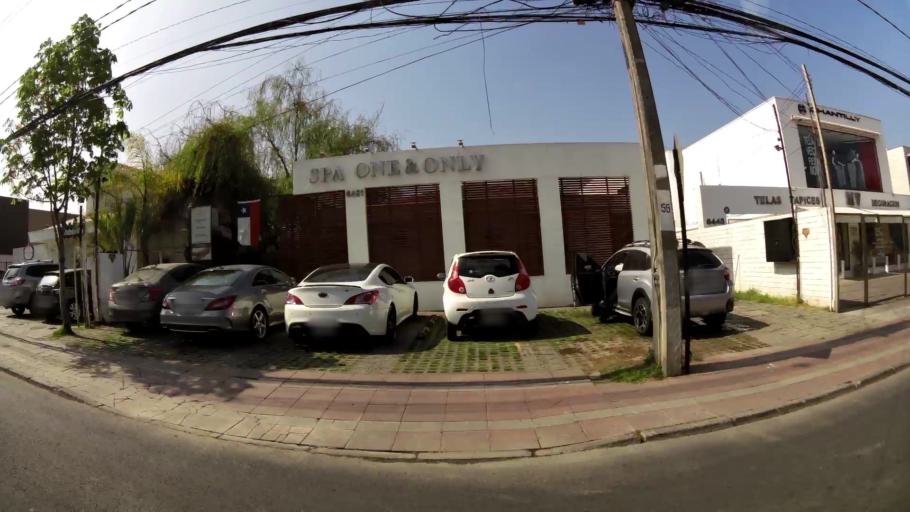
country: CL
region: Santiago Metropolitan
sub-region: Provincia de Santiago
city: Villa Presidente Frei, Nunoa, Santiago, Chile
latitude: -33.3826
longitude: -70.5722
